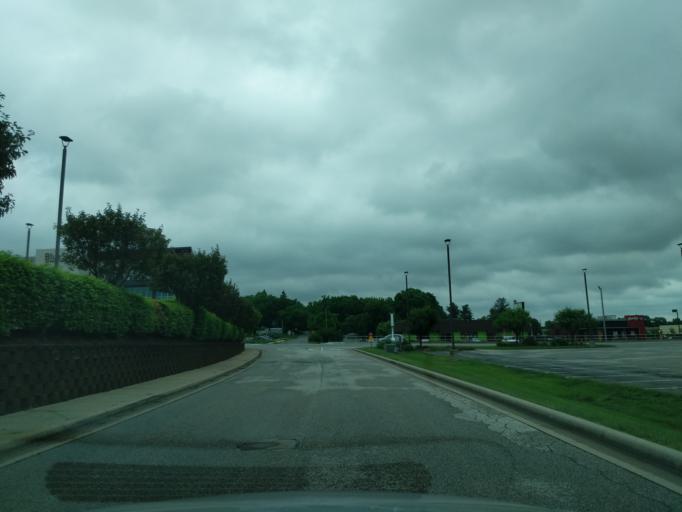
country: US
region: Indiana
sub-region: Hamilton County
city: Noblesville
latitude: 40.0462
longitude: -86.0219
